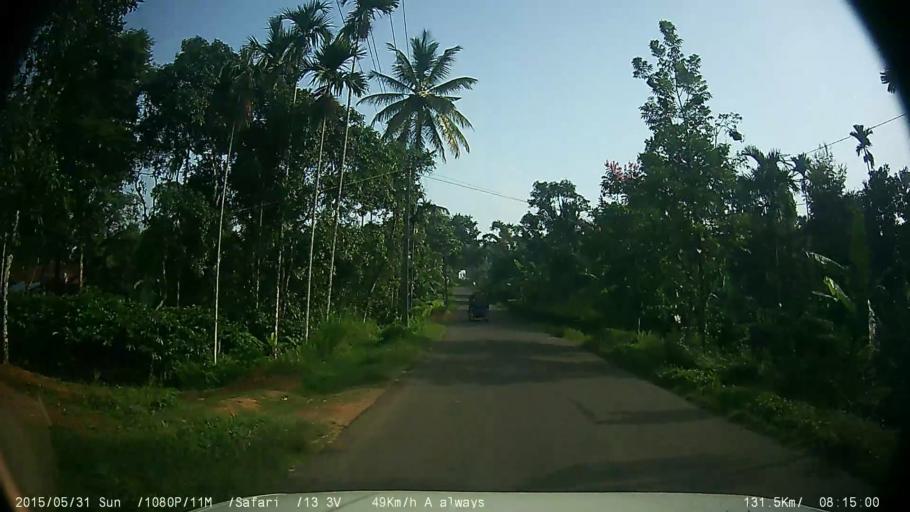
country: IN
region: Kerala
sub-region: Wayanad
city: Kalpetta
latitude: 11.6468
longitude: 76.0027
